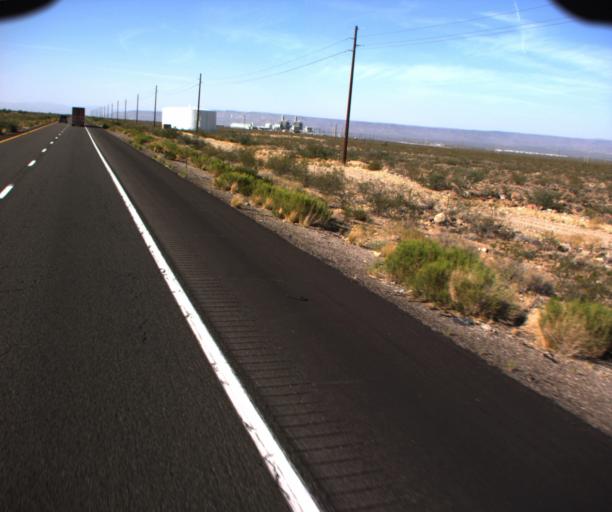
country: US
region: Arizona
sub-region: Mohave County
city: Kingman
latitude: 35.0683
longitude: -114.1243
